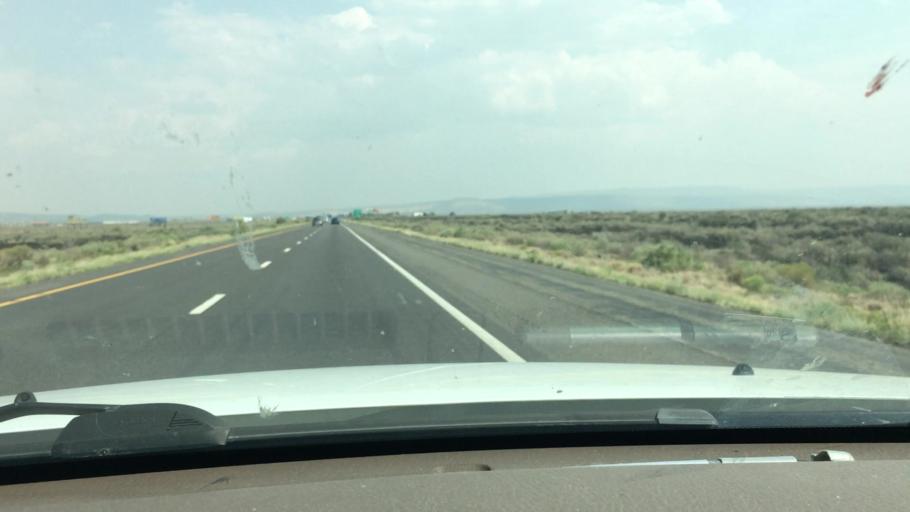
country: US
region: New Mexico
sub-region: Cibola County
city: Grants
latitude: 35.1366
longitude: -107.8466
